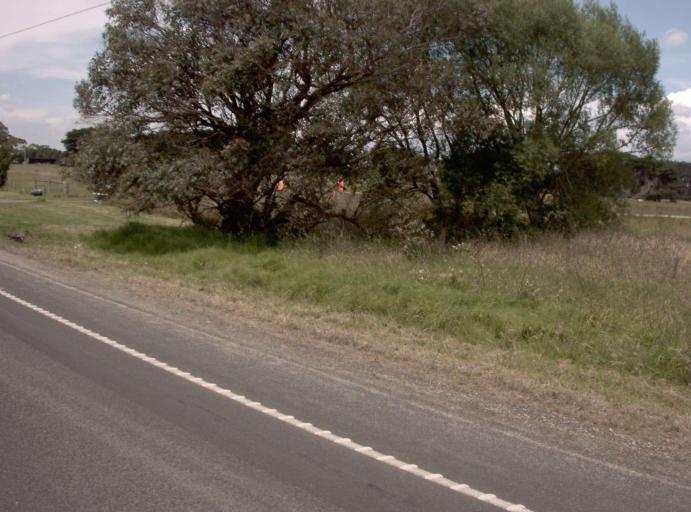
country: AU
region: Victoria
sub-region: Wellington
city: Sale
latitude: -38.0569
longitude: 147.0262
